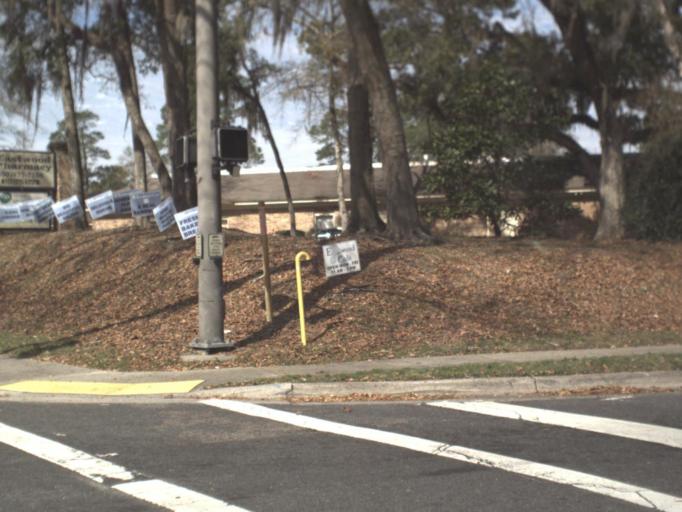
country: US
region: Florida
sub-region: Leon County
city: Tallahassee
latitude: 30.4571
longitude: -84.2367
